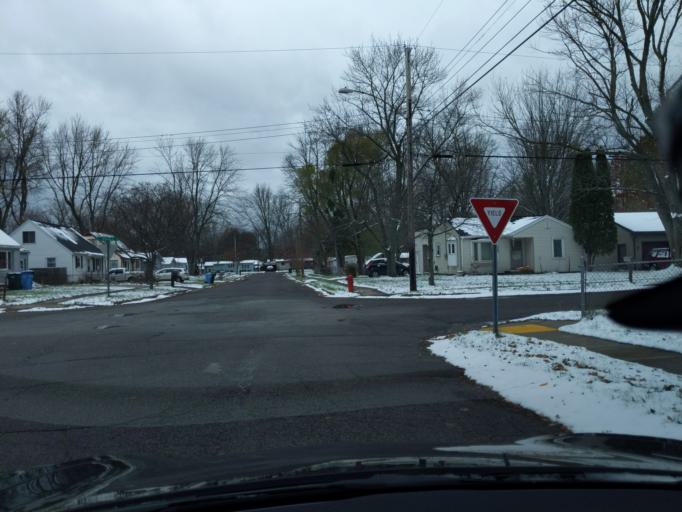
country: US
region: Michigan
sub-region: Ingham County
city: Lansing
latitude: 42.6893
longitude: -84.5909
